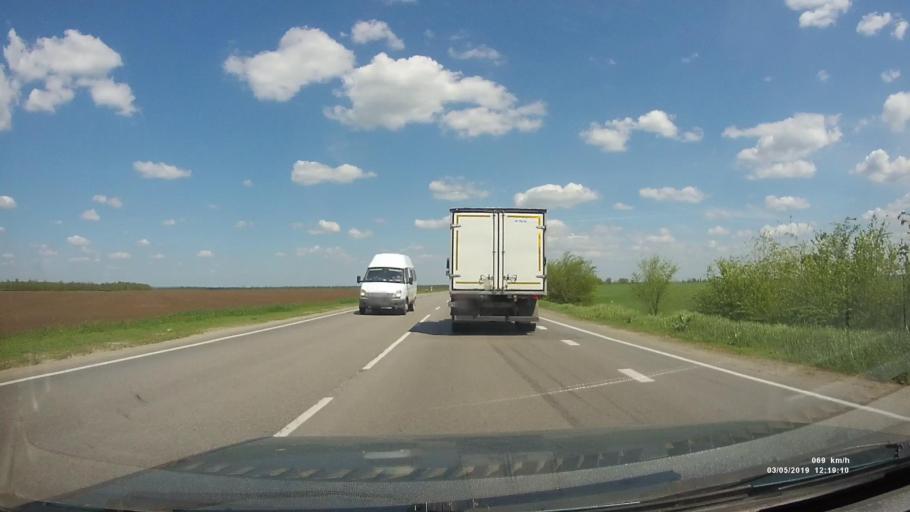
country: RU
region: Rostov
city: Melikhovskaya
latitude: 47.3989
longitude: 40.6055
